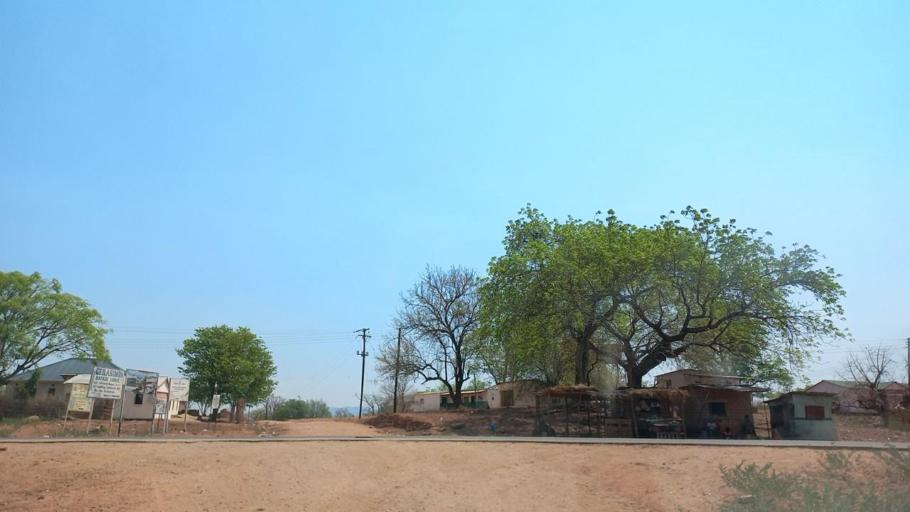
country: ZM
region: Lusaka
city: Luangwa
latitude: -15.6131
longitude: 30.3921
